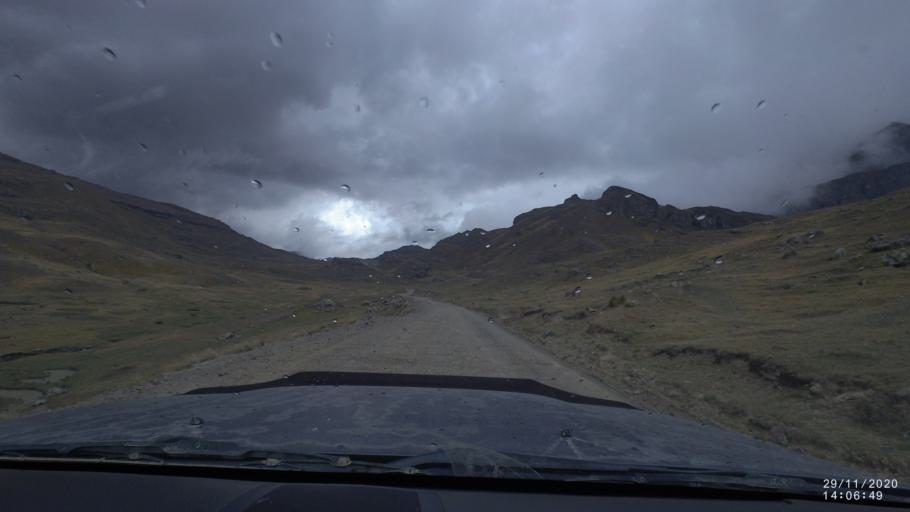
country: BO
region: Cochabamba
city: Sipe Sipe
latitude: -17.2162
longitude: -66.3800
